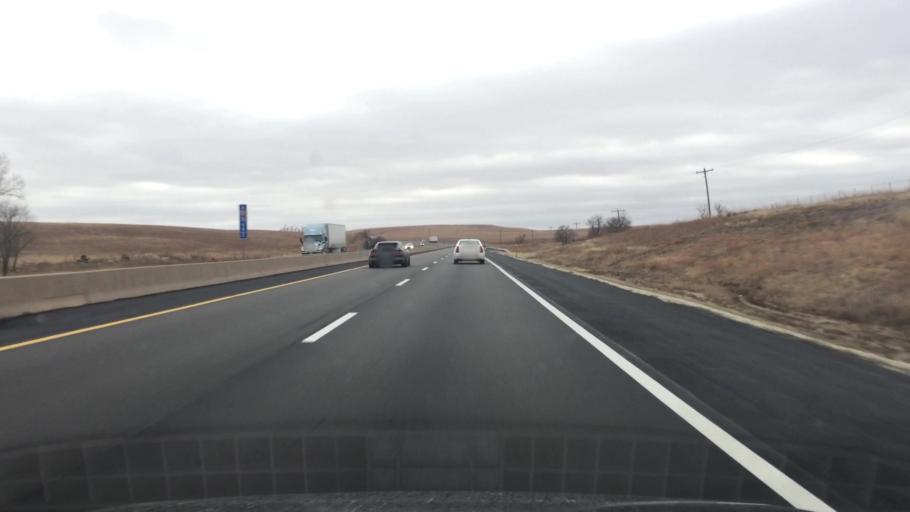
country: US
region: Kansas
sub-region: Chase County
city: Cottonwood Falls
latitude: 38.1213
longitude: -96.5592
